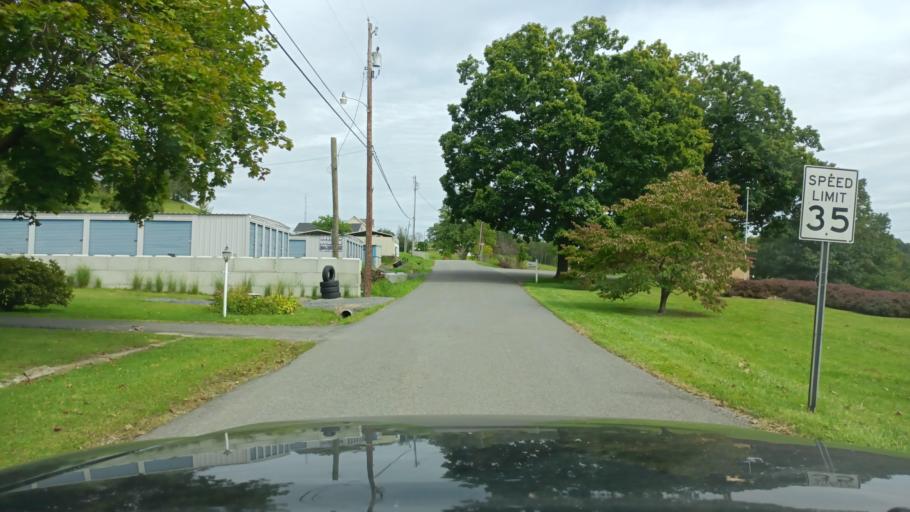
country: US
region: West Virginia
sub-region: Taylor County
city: Grafton
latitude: 39.3479
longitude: -80.0158
